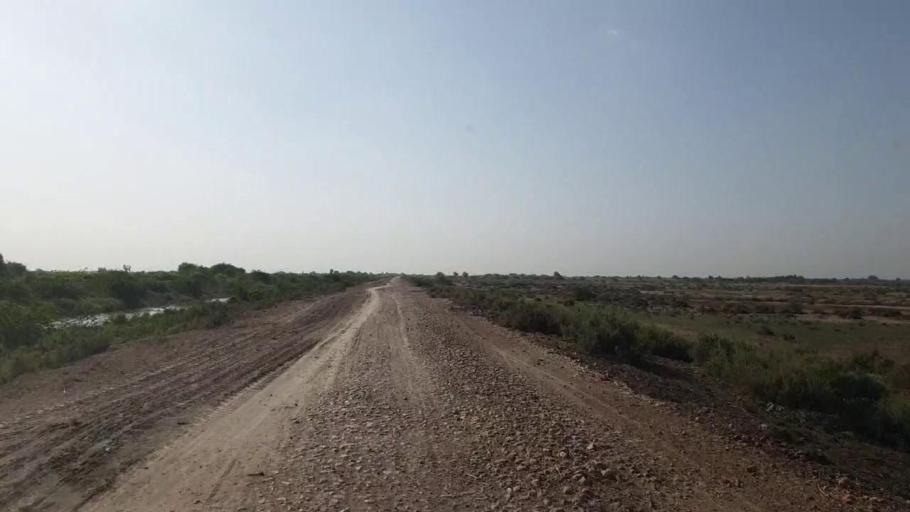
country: PK
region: Sindh
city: Kadhan
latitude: 24.6339
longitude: 69.0726
